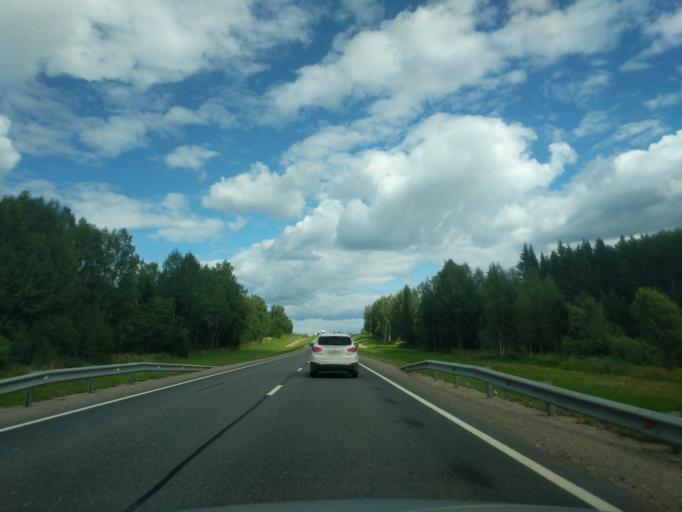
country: RU
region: Kostroma
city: Oktyabr'skiy
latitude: 57.7951
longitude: 41.1739
